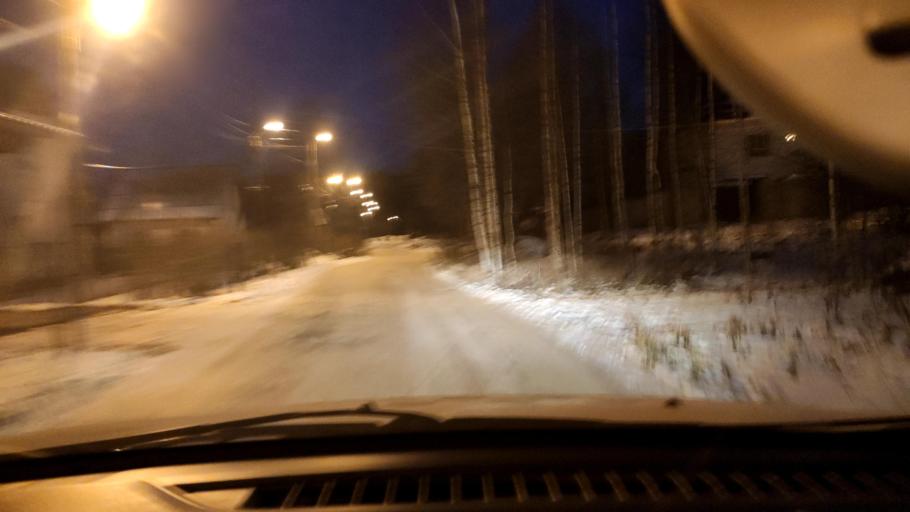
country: RU
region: Perm
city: Kondratovo
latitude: 58.0478
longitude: 56.1097
